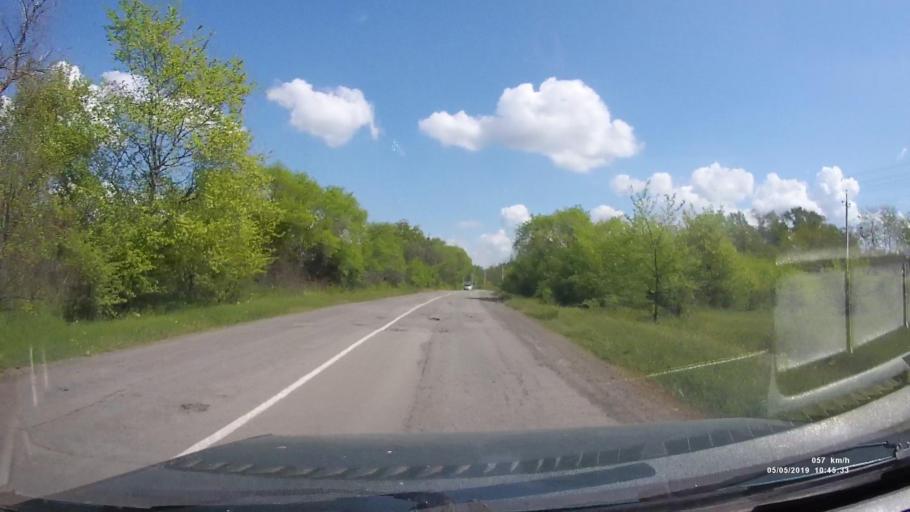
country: RU
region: Rostov
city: Ust'-Donetskiy
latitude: 47.6282
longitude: 40.8384
